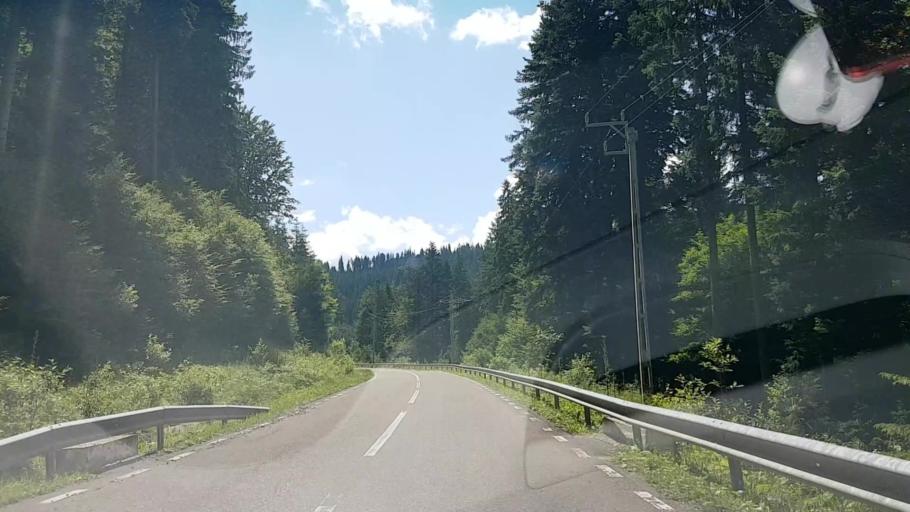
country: RO
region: Suceava
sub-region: Comuna Sadova
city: Sadova
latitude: 47.4703
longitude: 25.5128
